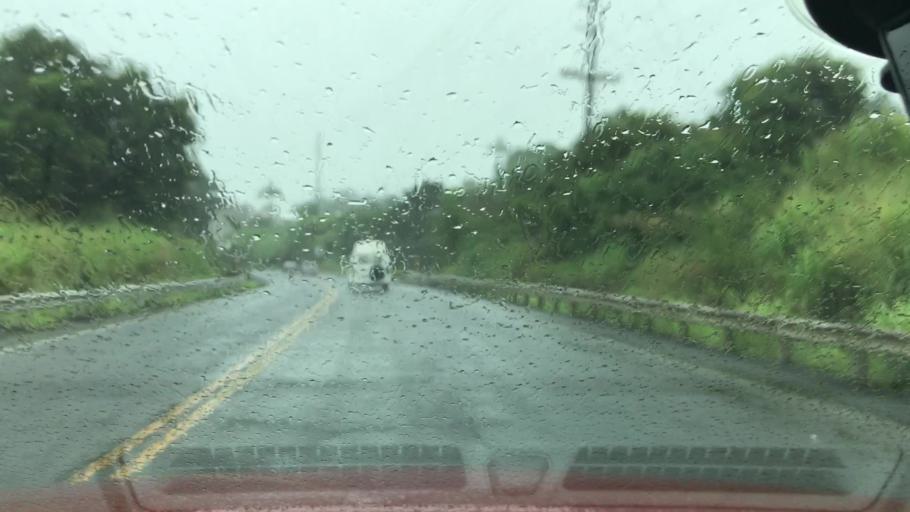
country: US
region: Hawaii
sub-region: Hawaii County
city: Pepeekeo
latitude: 19.9870
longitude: -155.2424
